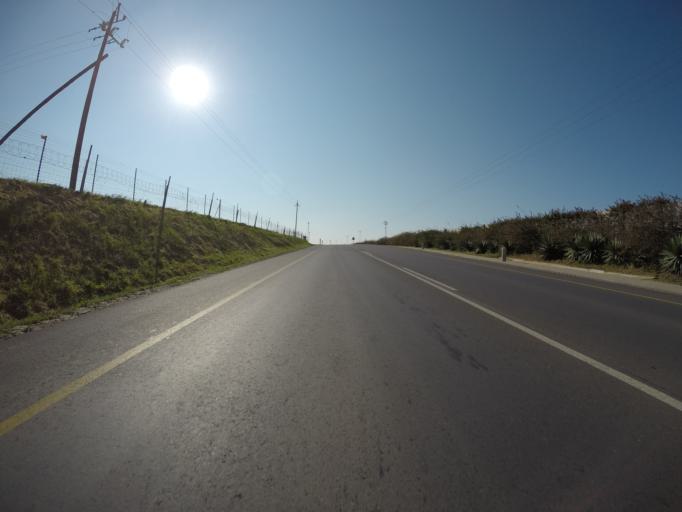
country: ZA
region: Western Cape
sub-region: Cape Winelands District Municipality
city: Noorder-Paarl
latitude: -33.6844
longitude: 18.9477
